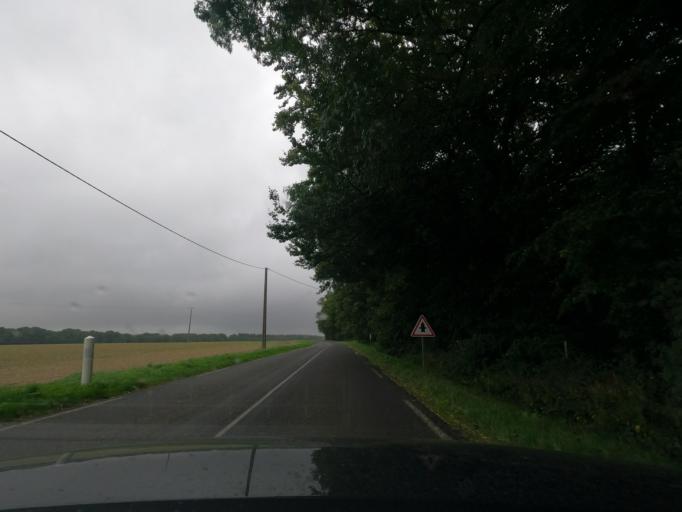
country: FR
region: Haute-Normandie
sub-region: Departement de la Seine-Maritime
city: Gaillefontaine
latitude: 49.6583
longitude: 1.6435
